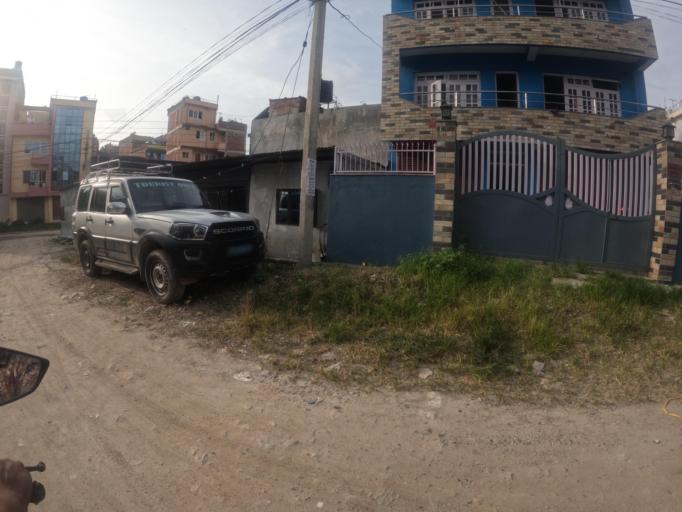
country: NP
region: Central Region
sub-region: Bagmati Zone
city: Bhaktapur
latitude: 27.6754
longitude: 85.3885
